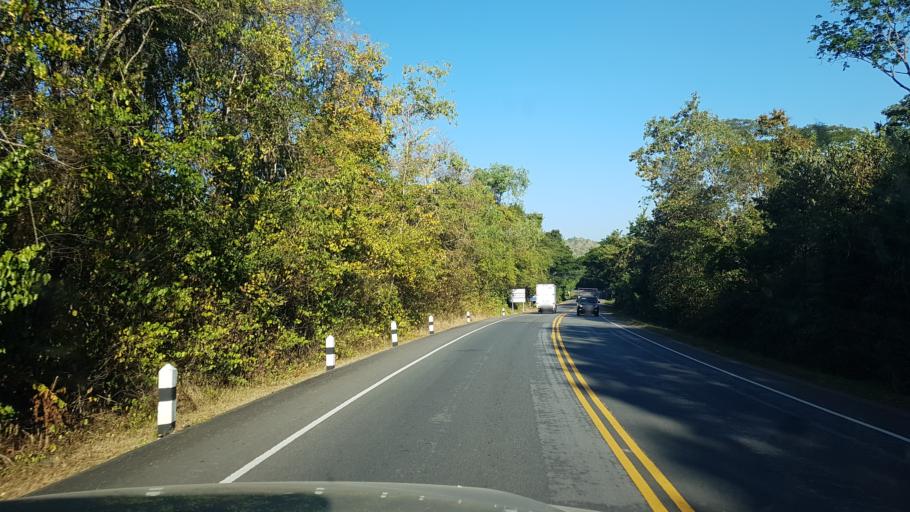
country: TH
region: Phetchabun
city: Nam Nao
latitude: 16.7591
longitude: 101.4671
